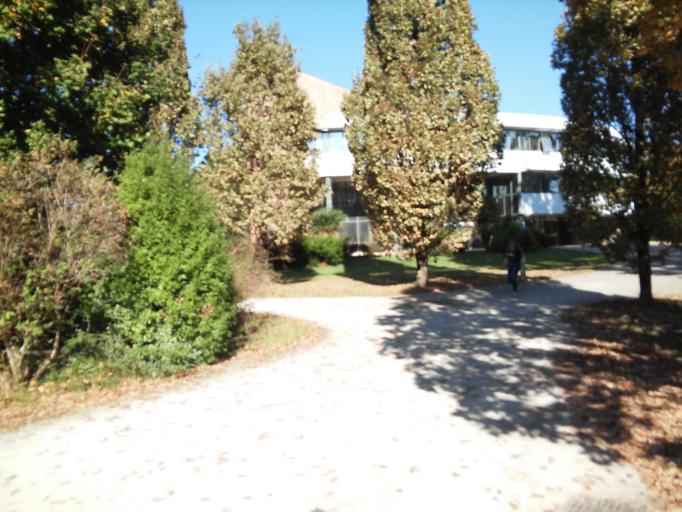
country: FR
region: Aquitaine
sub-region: Departement des Pyrenees-Atlantiques
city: Pau
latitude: 43.3132
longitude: -0.3656
